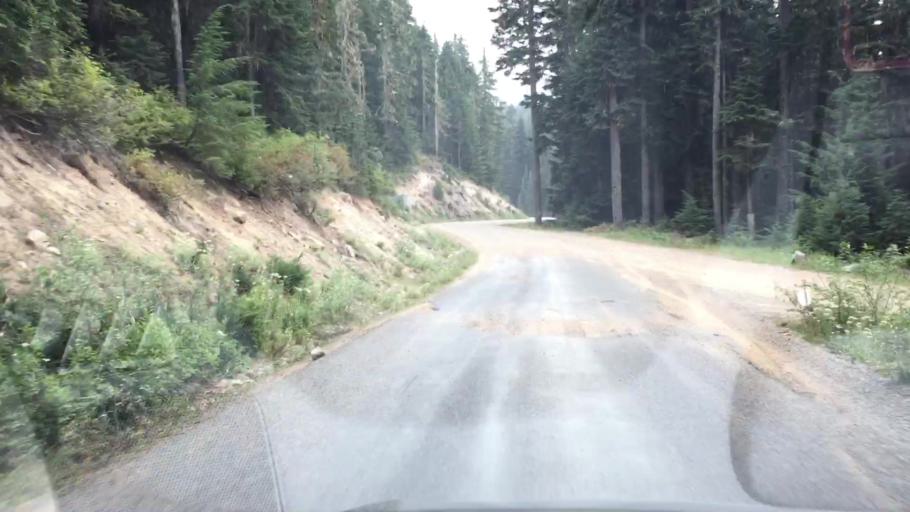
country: US
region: Washington
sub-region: Klickitat County
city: White Salmon
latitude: 46.2744
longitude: -121.6020
